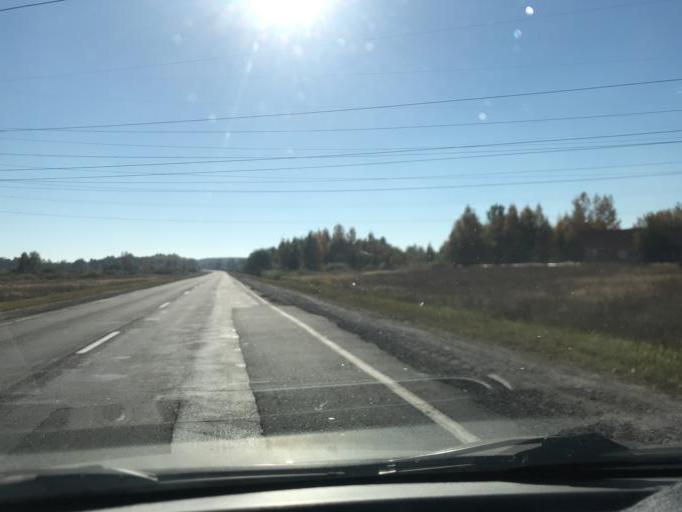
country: BY
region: Gomel
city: Kastsyukowka
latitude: 52.4491
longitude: 30.8250
